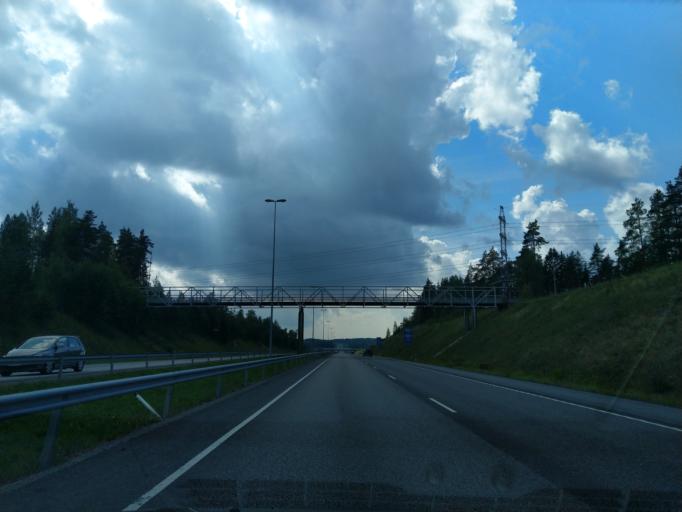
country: FI
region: South Karelia
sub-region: Imatra
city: Imatra
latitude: 61.1881
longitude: 28.7550
